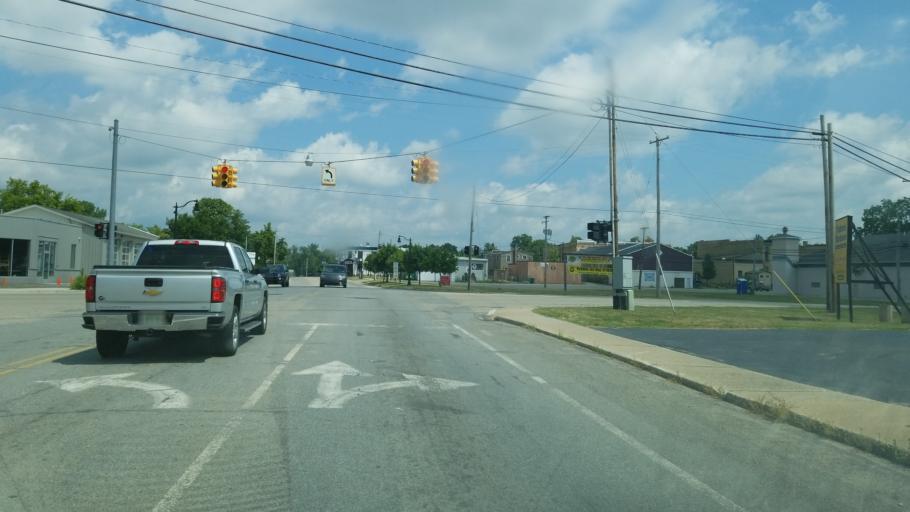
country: US
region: Michigan
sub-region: Montcalm County
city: Howard City
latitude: 43.3954
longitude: -85.4702
